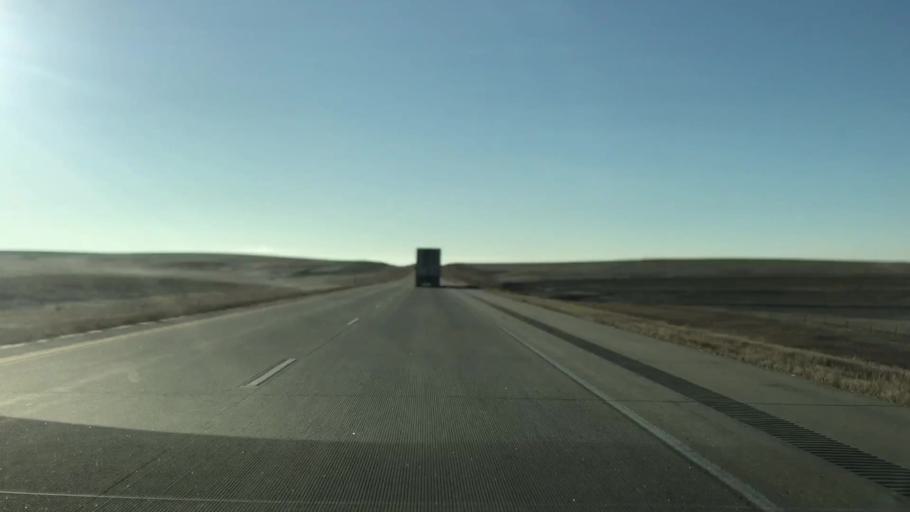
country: US
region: Colorado
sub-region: Lincoln County
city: Limon
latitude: 39.4003
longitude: -103.8989
